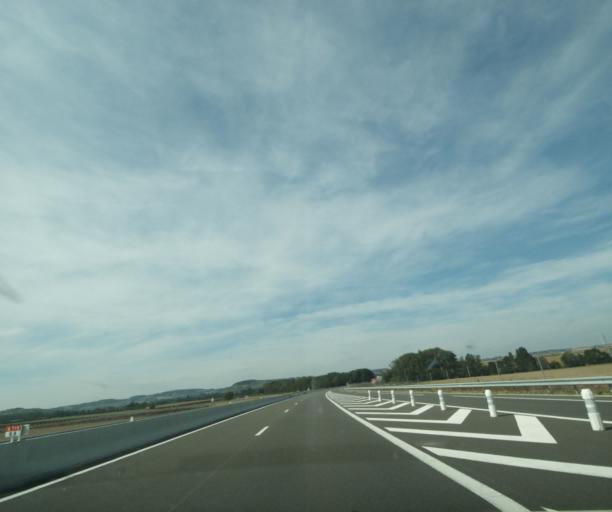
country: FR
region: Auvergne
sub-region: Departement de l'Allier
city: Gannat
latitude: 46.1029
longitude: 3.2337
